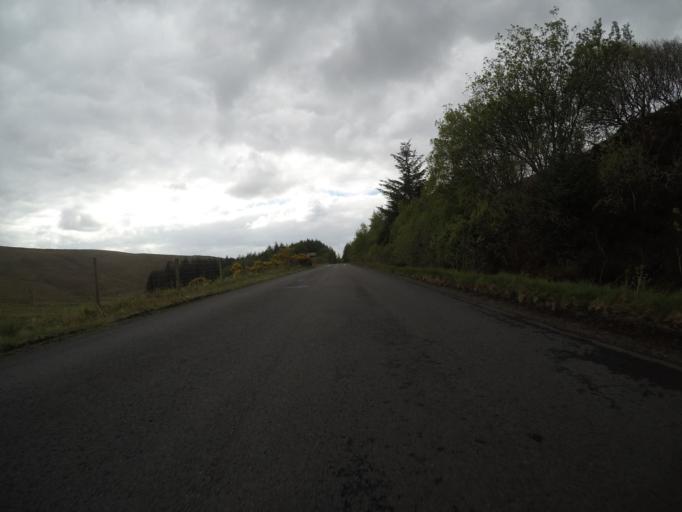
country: GB
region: Scotland
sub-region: Highland
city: Isle of Skye
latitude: 57.2971
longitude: -6.2830
